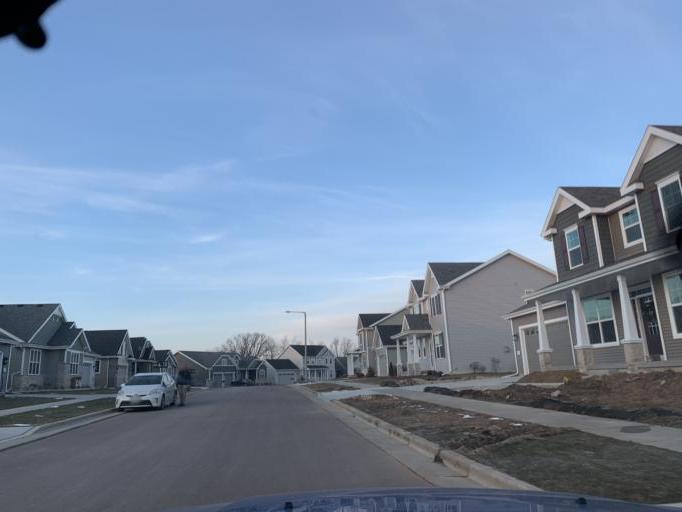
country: US
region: Wisconsin
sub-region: Dane County
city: Verona
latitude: 43.0553
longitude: -89.5649
